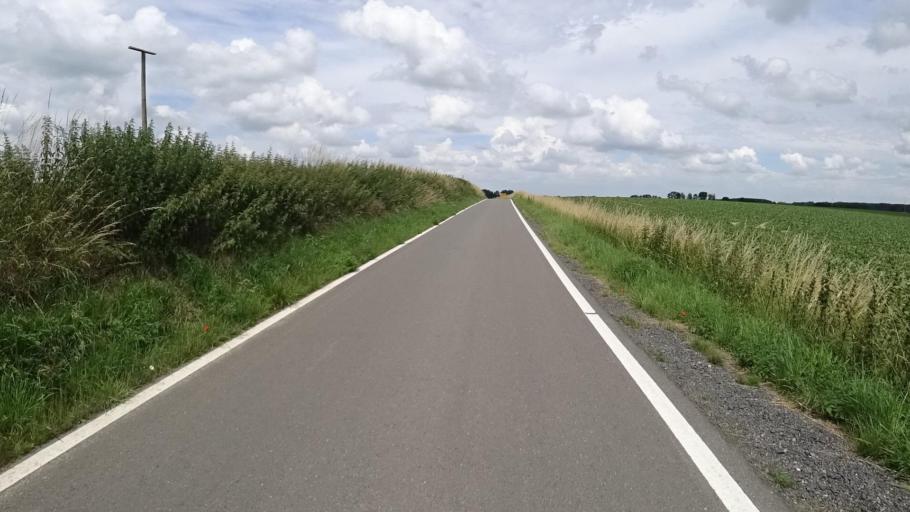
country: BE
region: Wallonia
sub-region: Province du Brabant Wallon
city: Perwez
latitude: 50.5528
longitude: 4.8324
